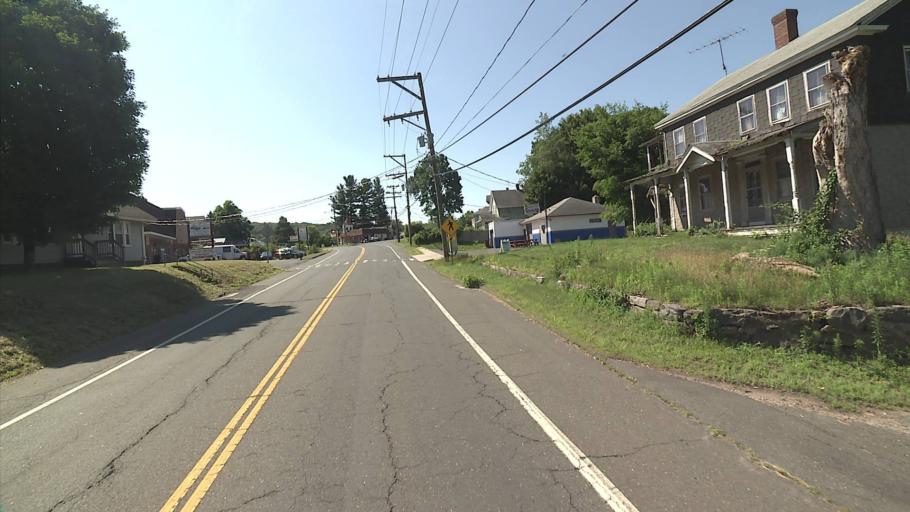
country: US
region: Connecticut
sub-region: Litchfield County
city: Terryville
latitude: 41.6718
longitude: -72.9926
